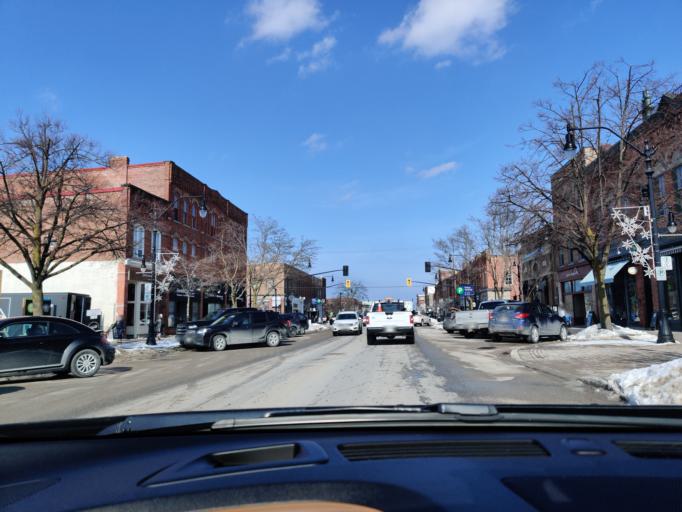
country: CA
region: Ontario
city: Collingwood
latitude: 44.5003
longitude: -80.2169
